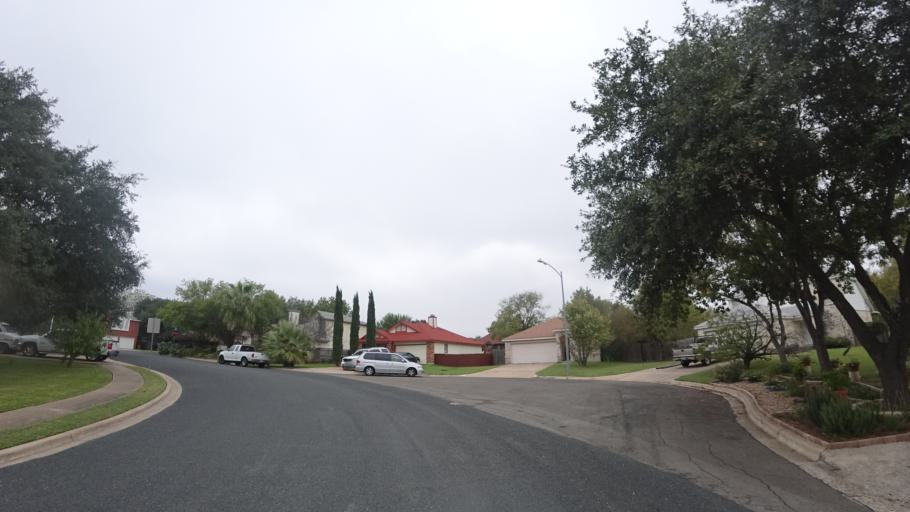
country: US
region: Texas
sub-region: Travis County
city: Pflugerville
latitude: 30.3915
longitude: -97.6540
